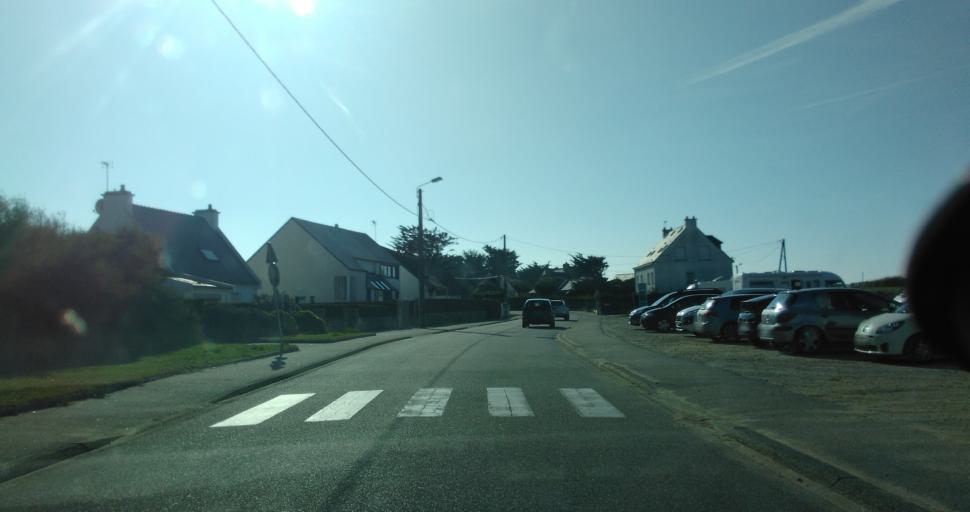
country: FR
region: Brittany
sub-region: Departement du Morbihan
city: Saint-Pierre-Quiberon
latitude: 47.5342
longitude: -3.1409
